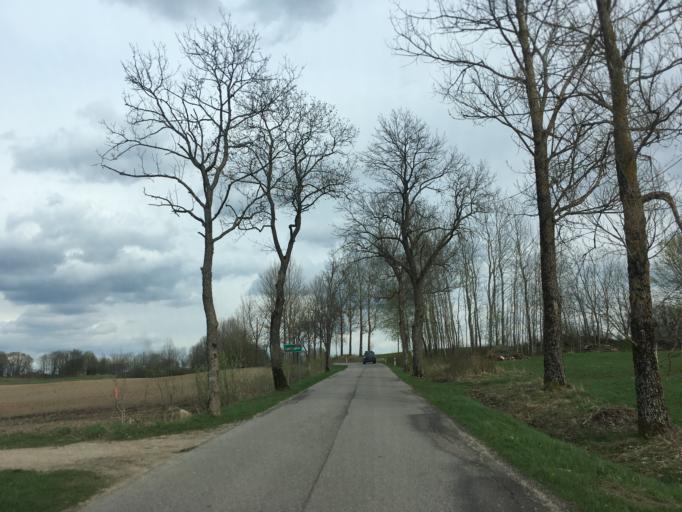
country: PL
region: Podlasie
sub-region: Powiat suwalski
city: Filipow
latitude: 54.3546
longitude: 22.7514
